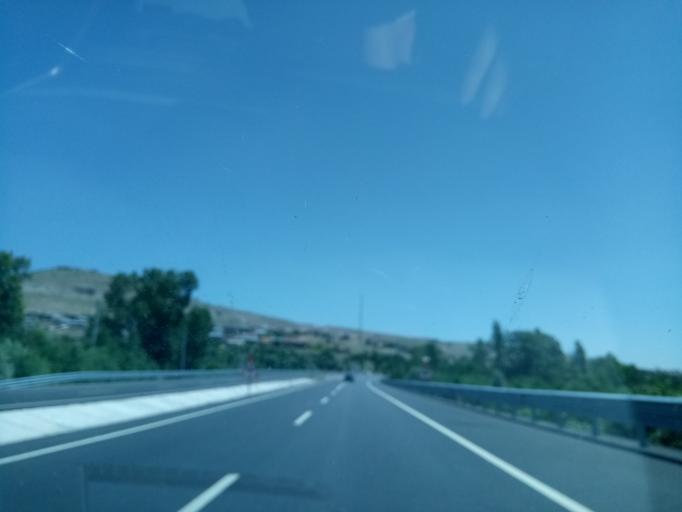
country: TR
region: Konya
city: Kiziloren
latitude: 37.7525
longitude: 32.1737
